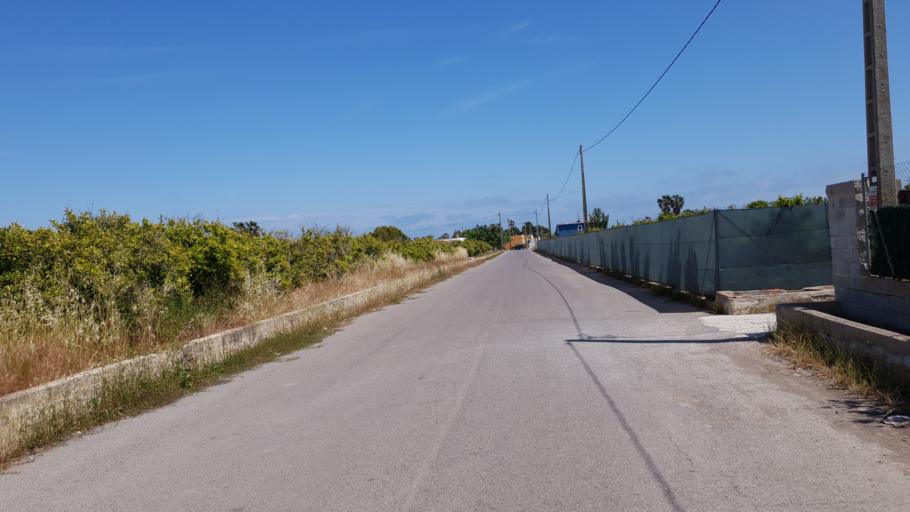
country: ES
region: Valencia
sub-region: Provincia de Castello
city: Burriana
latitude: 39.8603
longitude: -0.0894
